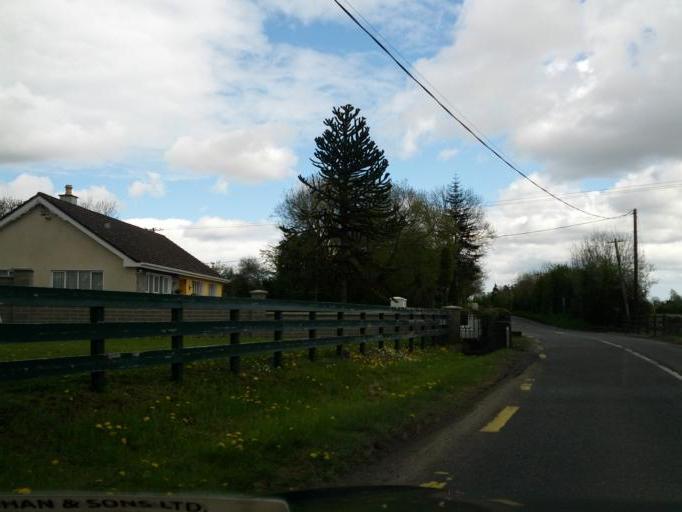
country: IE
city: Confey
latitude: 53.3755
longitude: -6.4813
